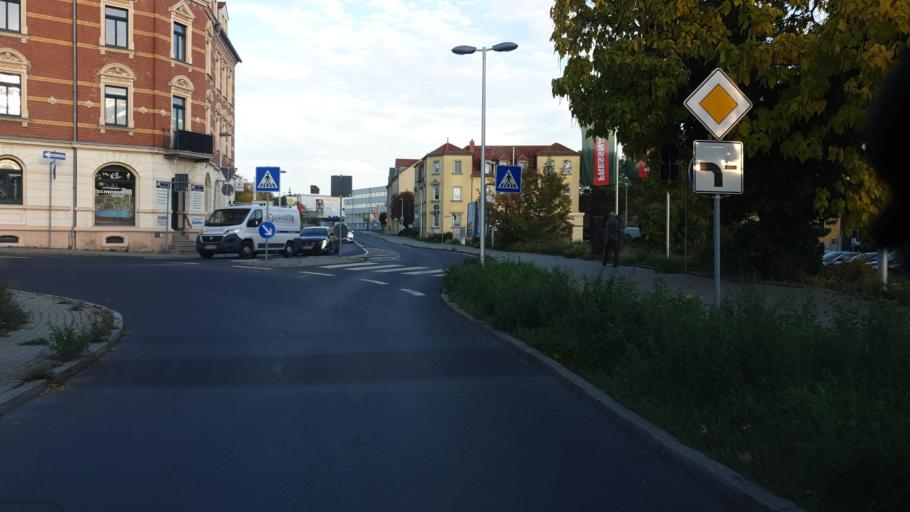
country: DE
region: Saxony
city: Meissen
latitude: 51.1670
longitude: 13.4926
